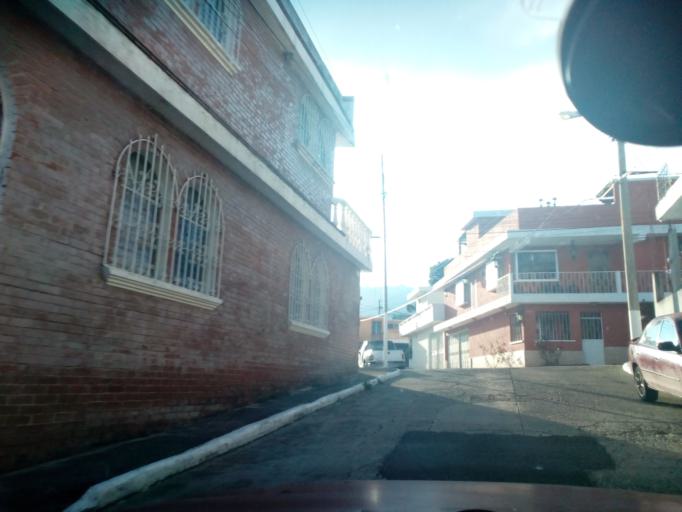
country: GT
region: Guatemala
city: Mixco
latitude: 14.6184
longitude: -90.5988
